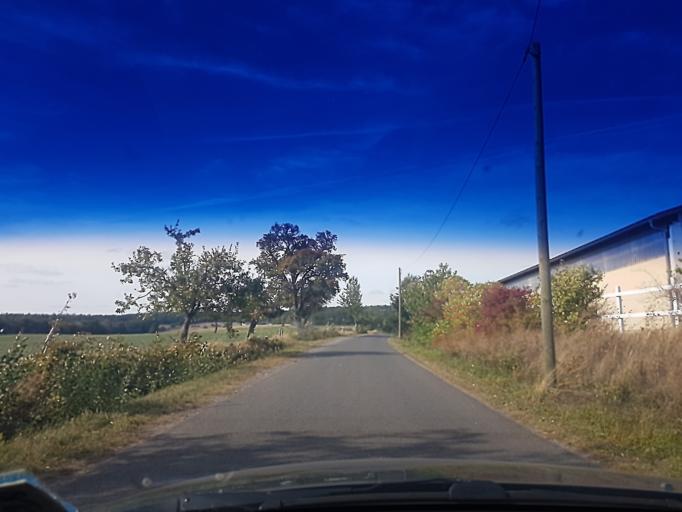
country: DE
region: Bavaria
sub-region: Regierungsbezirk Mittelfranken
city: Burghaslach
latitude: 49.7769
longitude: 10.5444
